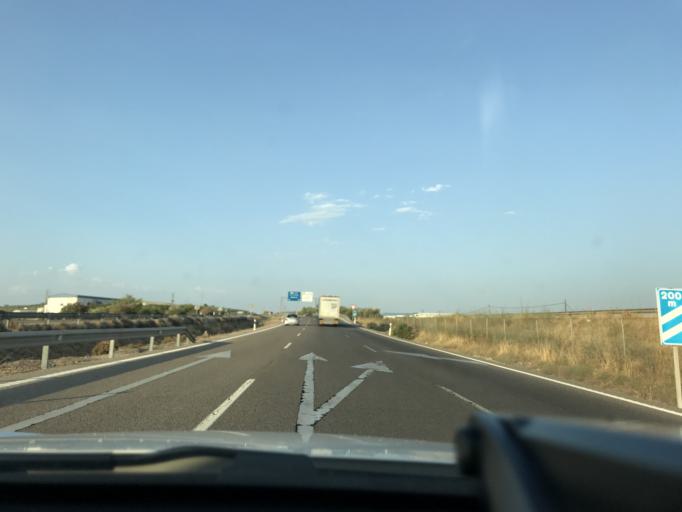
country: ES
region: Andalusia
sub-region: Provincia de Jaen
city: Bailen
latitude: 38.0926
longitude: -3.8127
